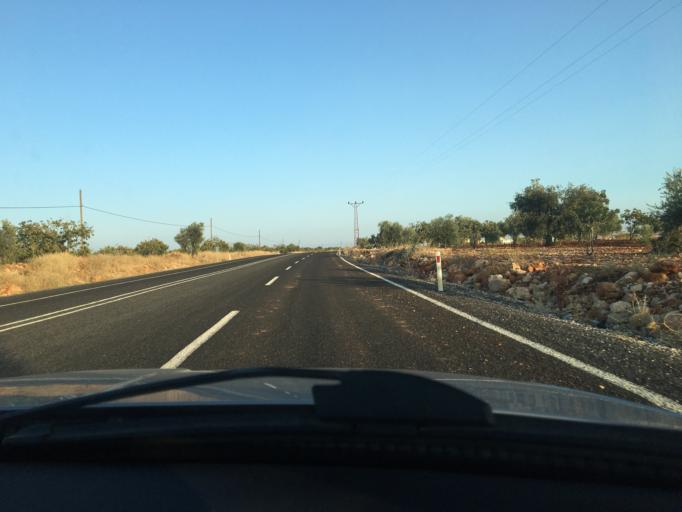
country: TR
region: Sanliurfa
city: Halfeti
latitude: 37.2442
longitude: 37.8974
